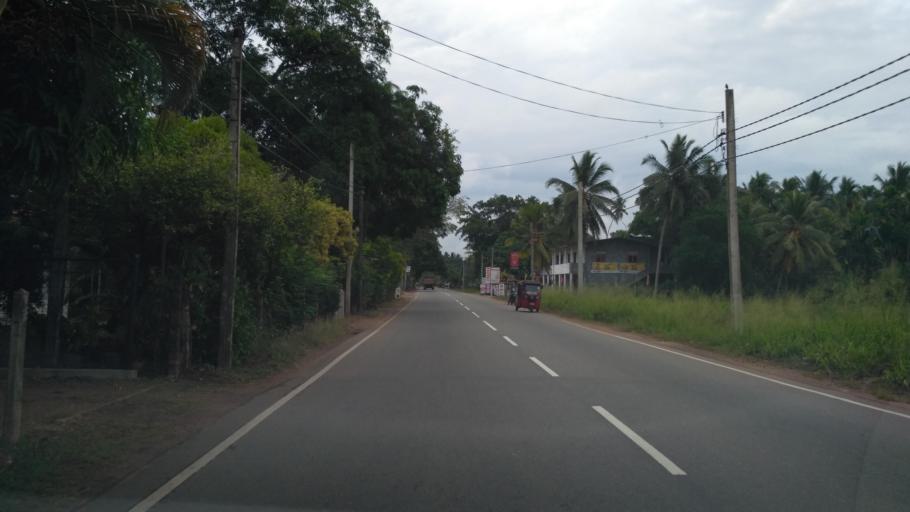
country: LK
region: North Western
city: Kuliyapitiya
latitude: 7.3256
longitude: 80.0349
